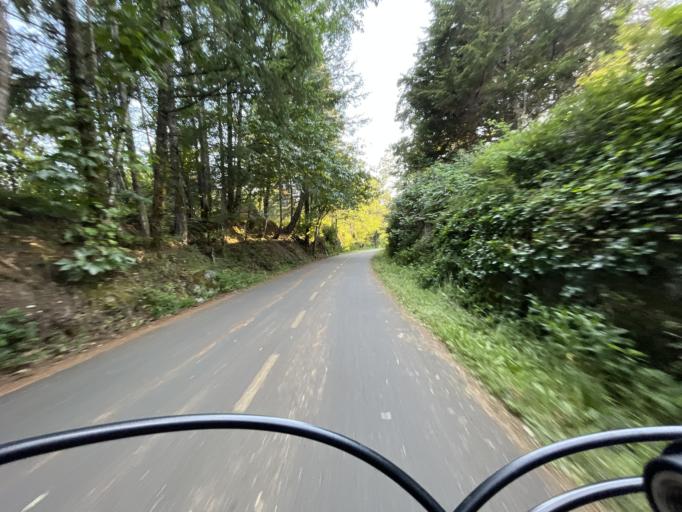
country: CA
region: British Columbia
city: Colwood
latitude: 48.4489
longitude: -123.4703
